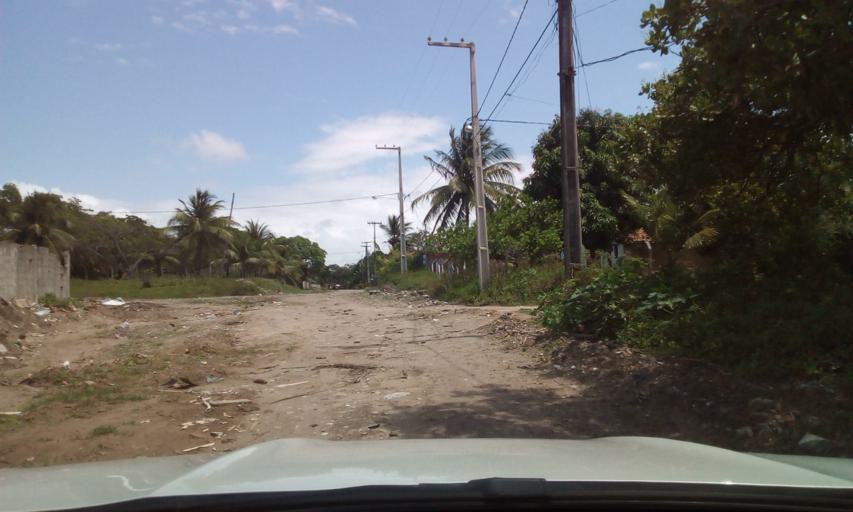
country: BR
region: Paraiba
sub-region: Joao Pessoa
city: Joao Pessoa
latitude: -7.1476
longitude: -34.8065
